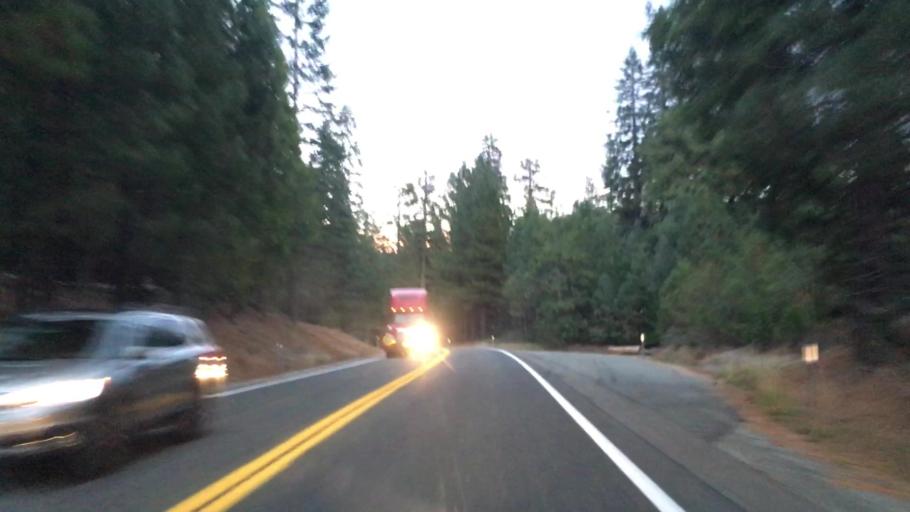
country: US
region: California
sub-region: El Dorado County
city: South Lake Tahoe
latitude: 38.7903
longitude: -120.1867
